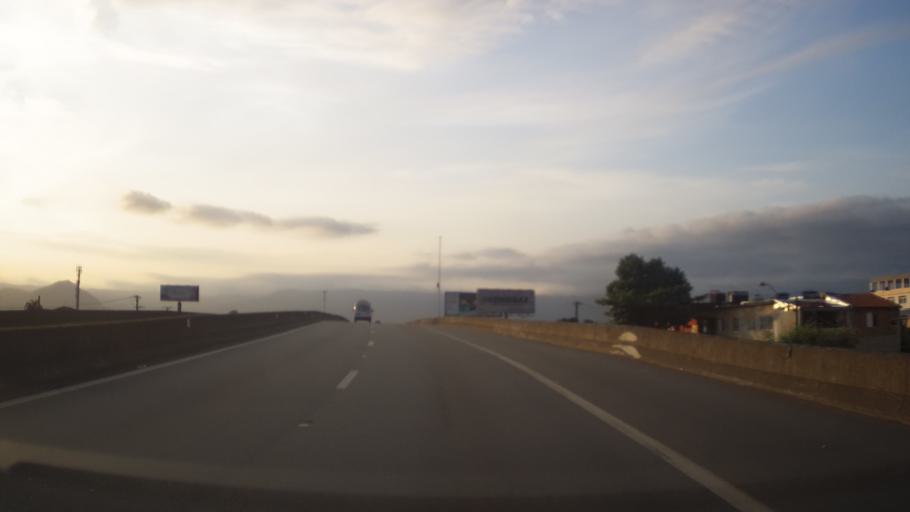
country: BR
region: Sao Paulo
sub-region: Sao Vicente
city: Sao Vicente
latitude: -23.9661
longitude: -46.4005
